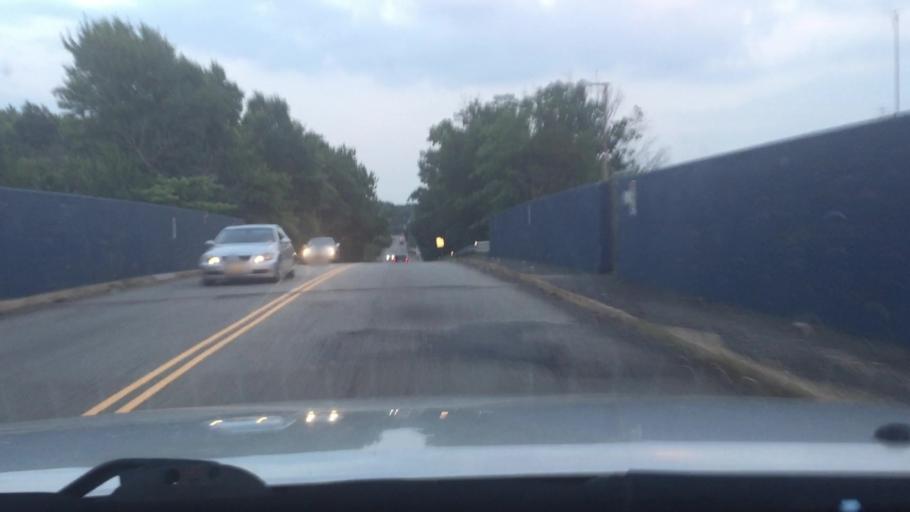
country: US
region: New Jersey
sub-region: Middlesex County
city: Milltown
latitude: 40.4478
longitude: -74.4910
